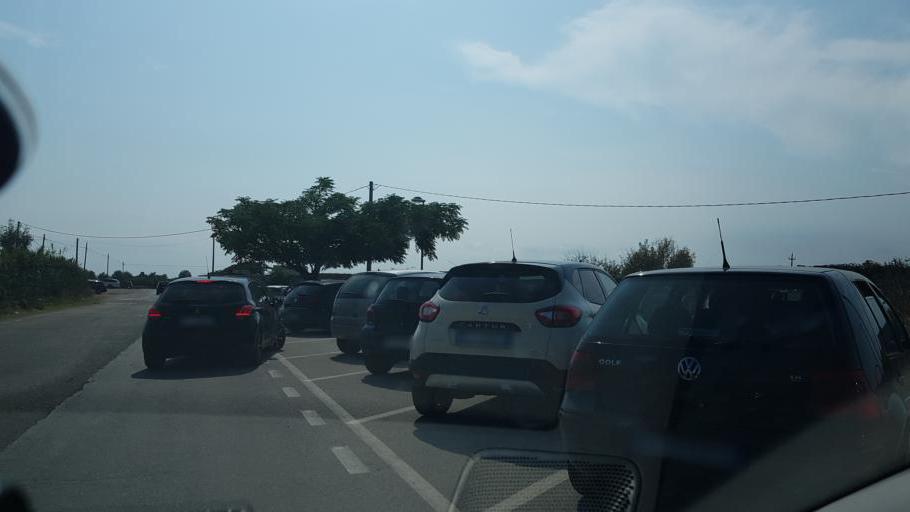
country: IT
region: Apulia
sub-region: Provincia di Bari
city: Monopoli
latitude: 40.9382
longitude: 17.3175
